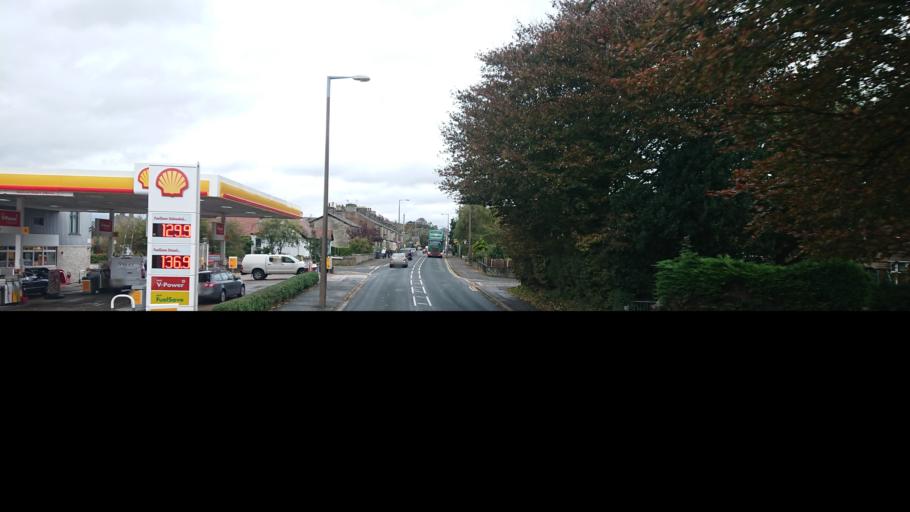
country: GB
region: England
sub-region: Lancashire
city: Lancaster
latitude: 54.0253
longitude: -2.7951
